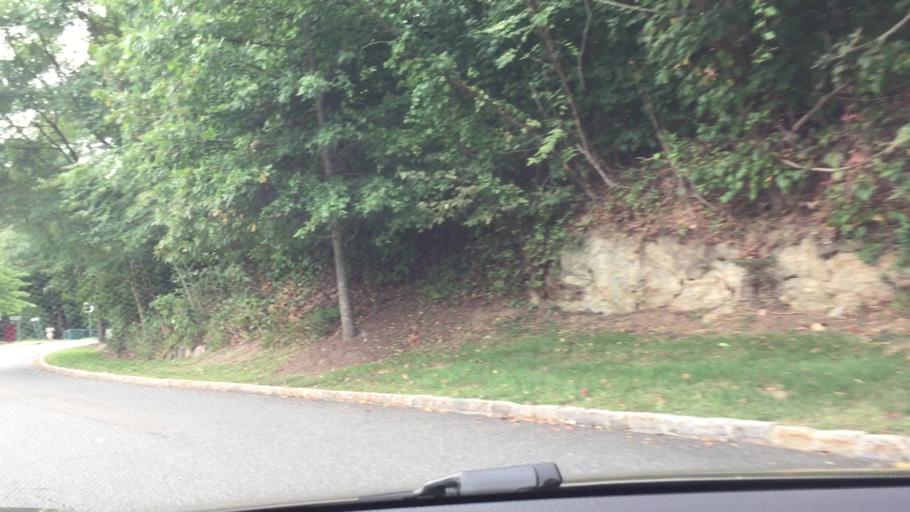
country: US
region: New York
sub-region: Westchester County
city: Purchase
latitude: 41.0297
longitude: -73.7298
